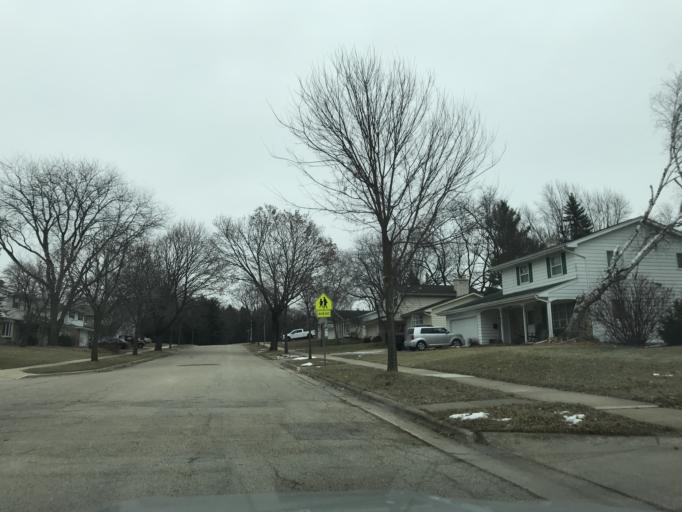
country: US
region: Wisconsin
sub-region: Dane County
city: Monona
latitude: 43.0955
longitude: -89.3000
